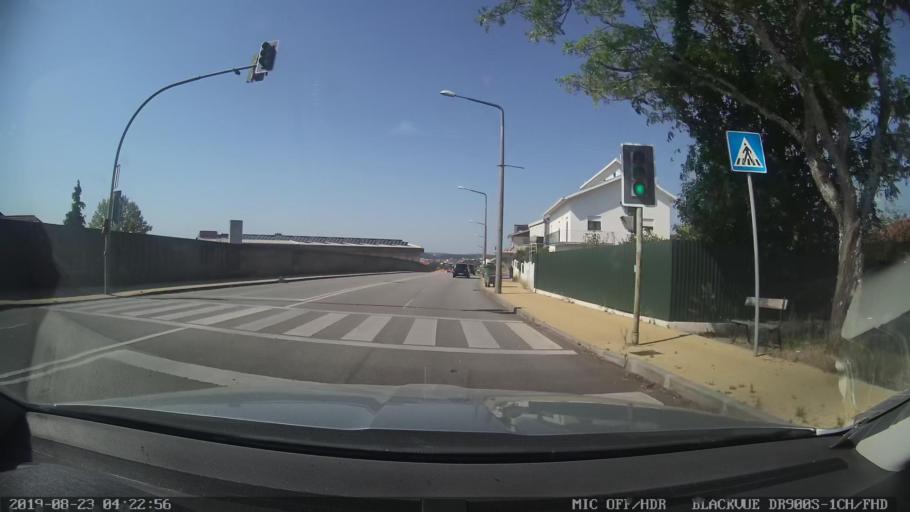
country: PT
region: Coimbra
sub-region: Coimbra
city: Coimbra
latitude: 40.2193
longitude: -8.4070
